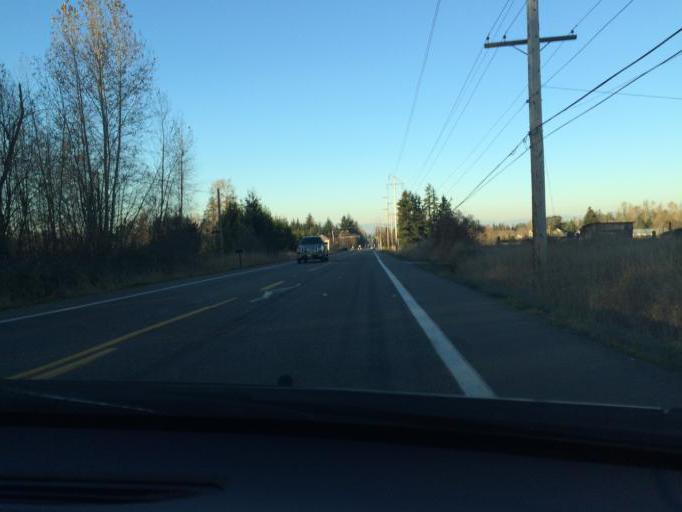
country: US
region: Washington
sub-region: Whatcom County
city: Bellingham
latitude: 48.8305
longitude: -122.4430
